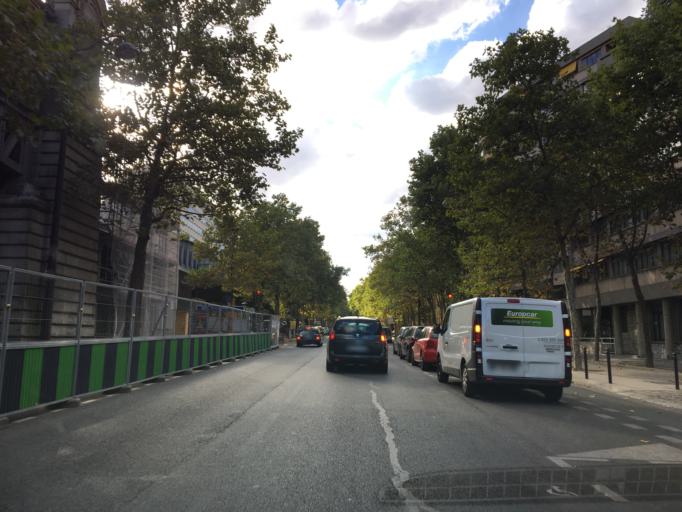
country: FR
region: Ile-de-France
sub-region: Departement du Val-de-Marne
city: Gentilly
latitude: 48.8313
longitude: 2.3435
